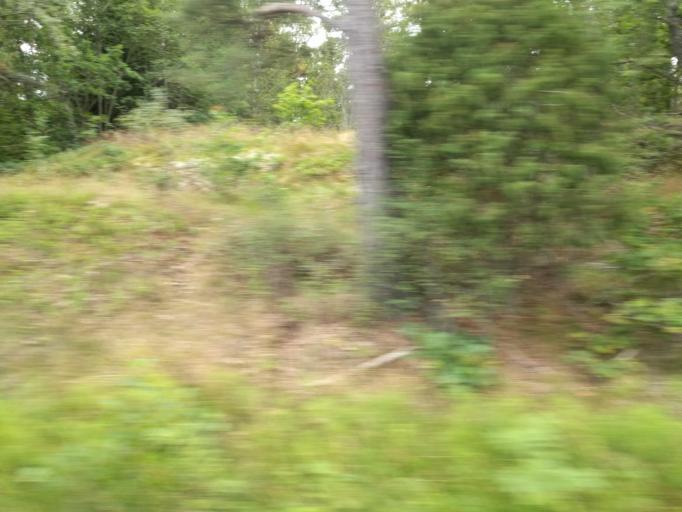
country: SE
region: Soedermanland
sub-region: Oxelosunds Kommun
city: Bara
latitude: 58.4872
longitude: 16.9136
